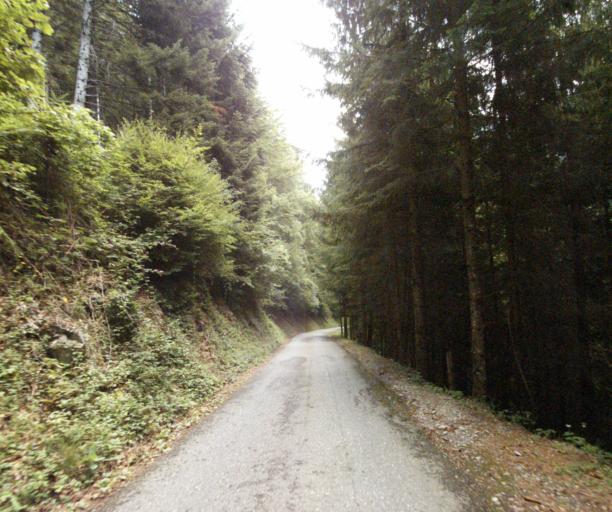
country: CH
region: Vaud
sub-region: Aigle District
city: Villeneuve
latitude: 46.4100
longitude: 6.9427
